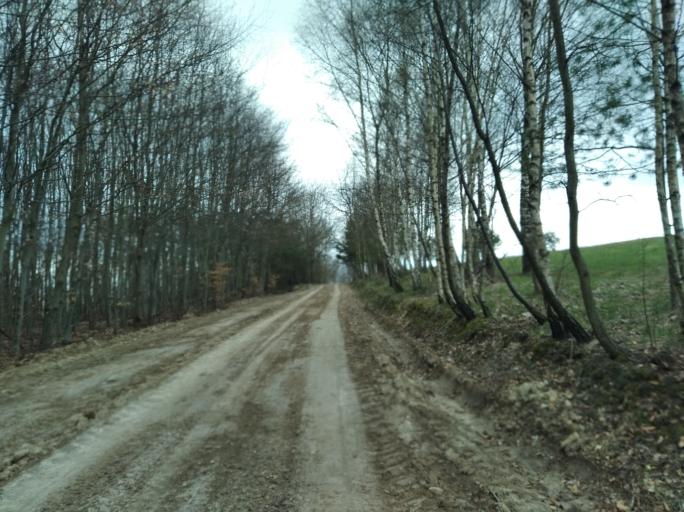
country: PL
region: Subcarpathian Voivodeship
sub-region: Powiat strzyzowski
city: Jawornik
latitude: 49.8213
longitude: 21.9037
